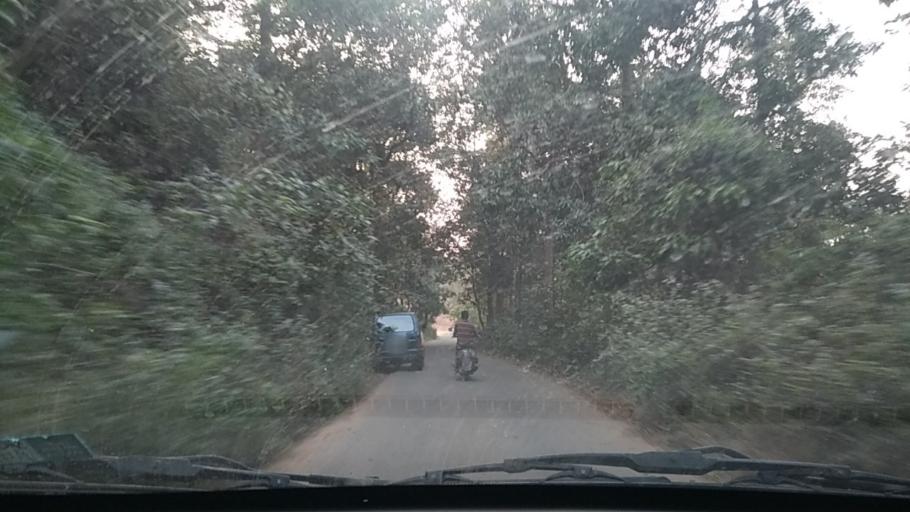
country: IN
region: Goa
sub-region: South Goa
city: Sancoale
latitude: 15.3499
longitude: 73.9435
